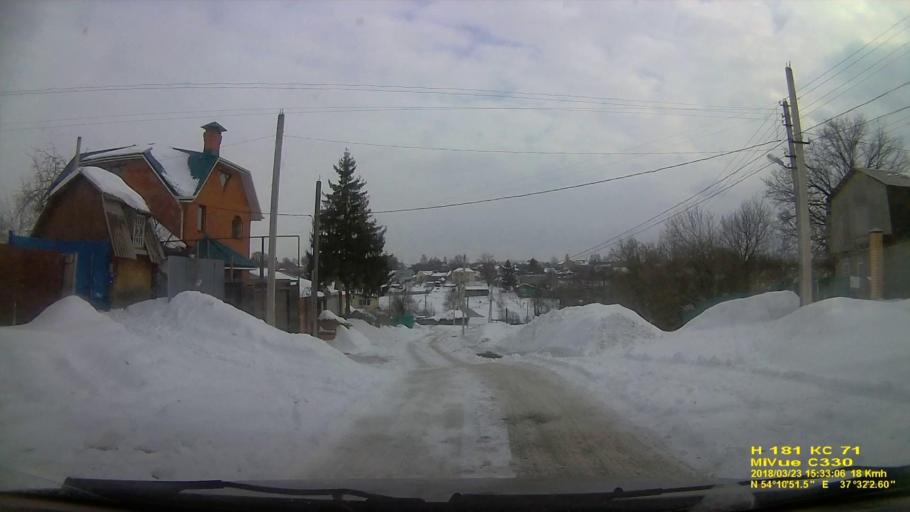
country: RU
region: Tula
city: Kosaya Gora
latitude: 54.1809
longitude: 37.5341
